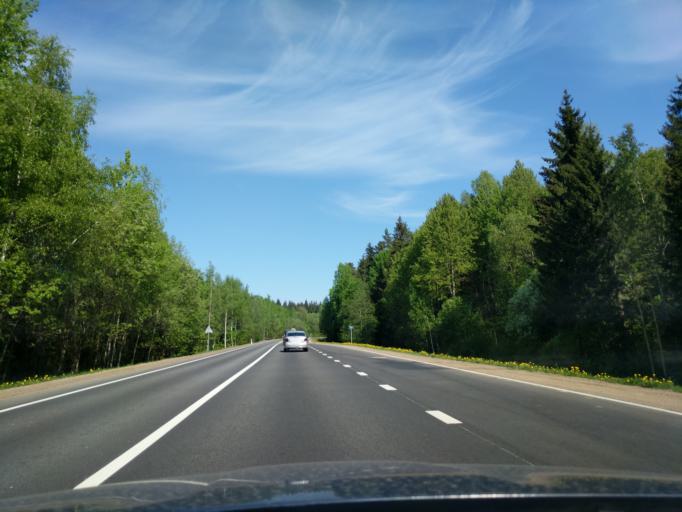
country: BY
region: Minsk
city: Bal'shavik
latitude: 54.1035
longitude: 27.5313
